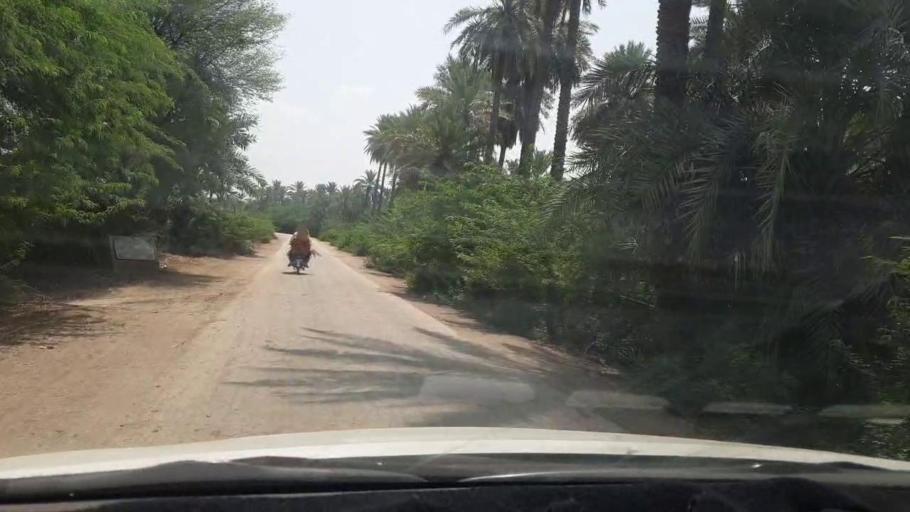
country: PK
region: Sindh
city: Khairpur
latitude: 27.5365
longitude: 68.8823
